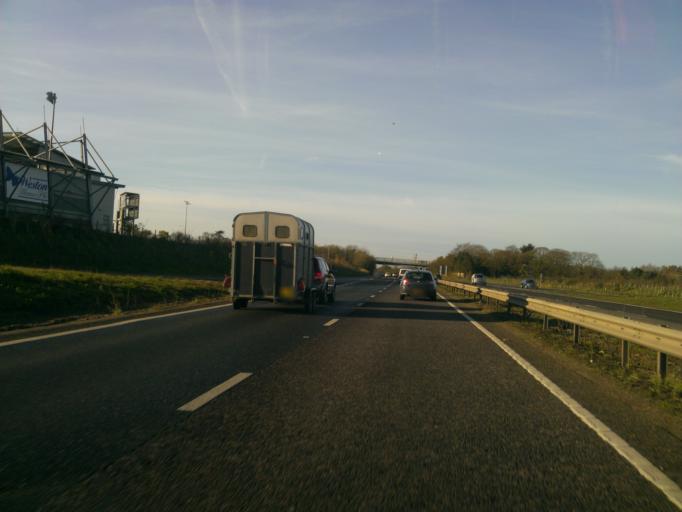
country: GB
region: England
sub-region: Essex
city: Great Horkesley
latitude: 51.9247
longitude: 0.8989
